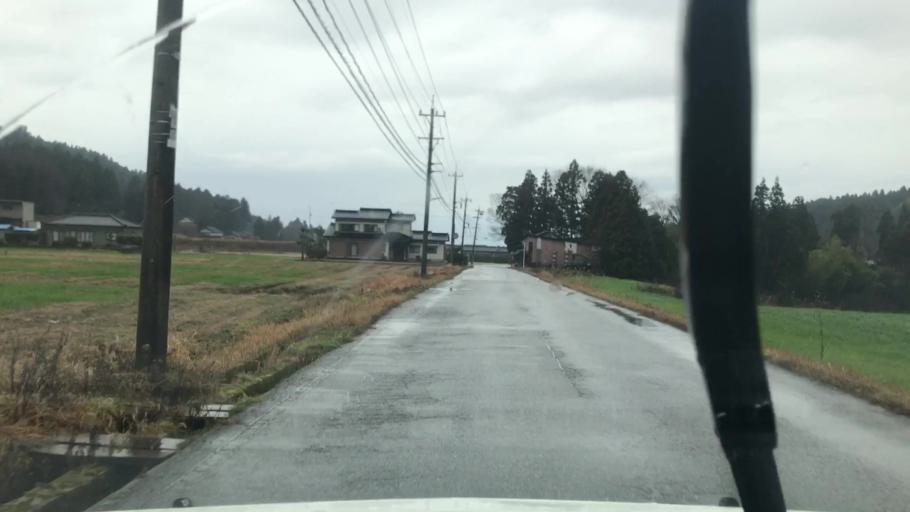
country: JP
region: Toyama
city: Kamiichi
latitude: 36.6008
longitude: 137.2990
